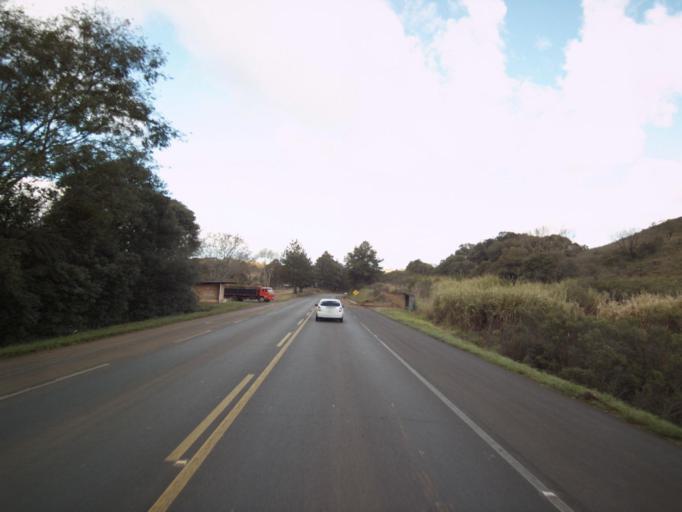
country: BR
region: Santa Catarina
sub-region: Campos Novos
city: Campos Novos
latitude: -27.3221
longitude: -51.3618
